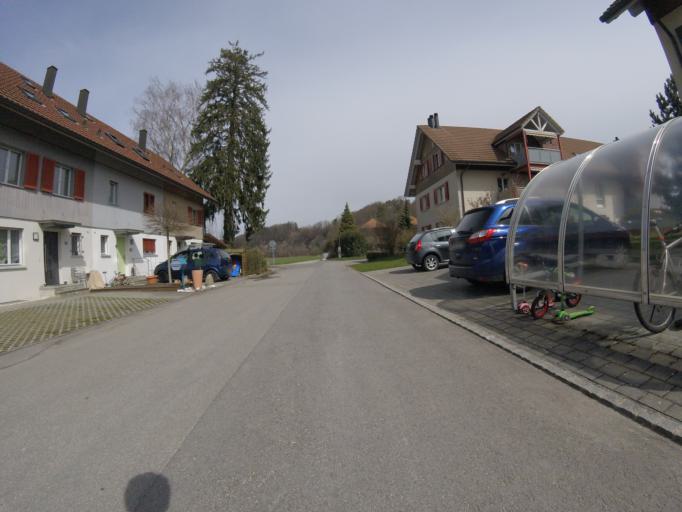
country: CH
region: Bern
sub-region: Bern-Mittelland District
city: Laupen
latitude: 46.9109
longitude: 7.2405
